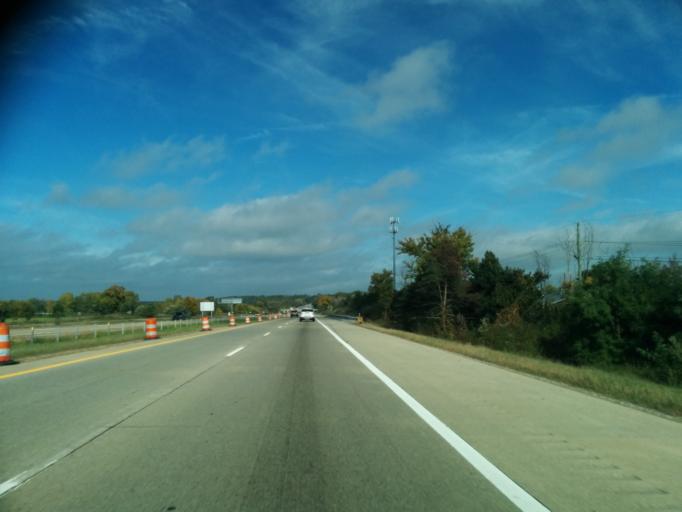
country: US
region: Michigan
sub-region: Livingston County
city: Brighton
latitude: 42.6472
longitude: -83.7548
